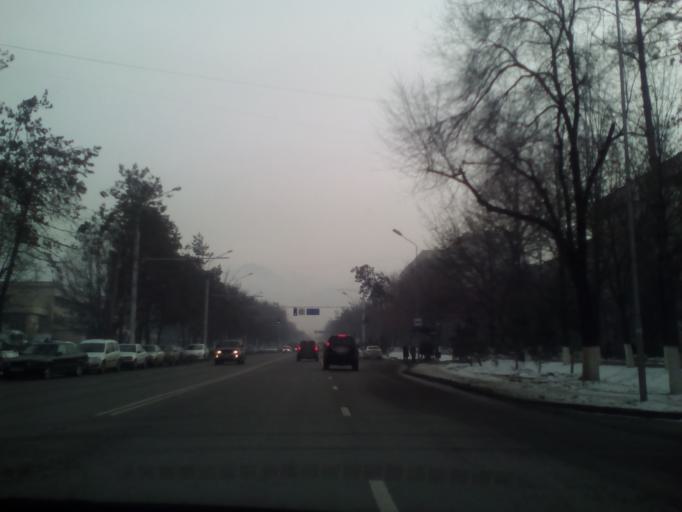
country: KZ
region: Almaty Qalasy
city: Almaty
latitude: 43.2359
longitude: 76.8308
